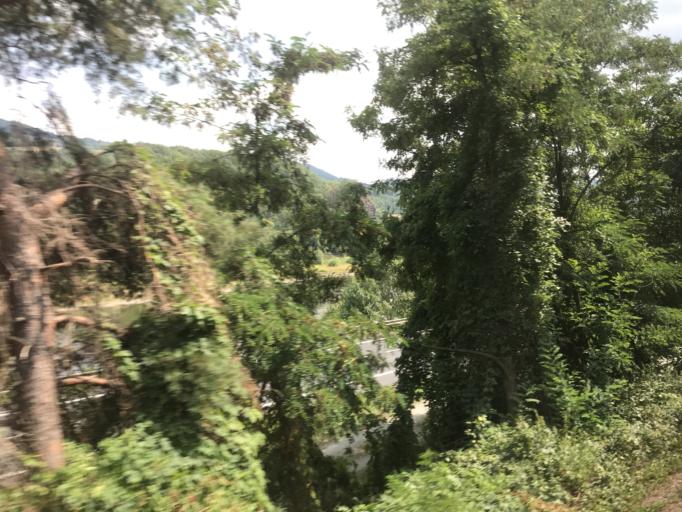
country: CZ
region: Ustecky
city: Povrly
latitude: 50.7256
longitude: 14.1855
